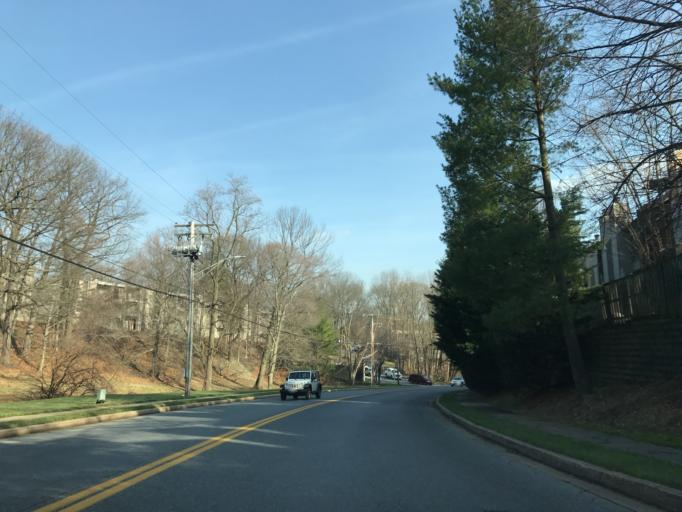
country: US
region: Maryland
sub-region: Baltimore County
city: Lutherville
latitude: 39.3762
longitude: -76.6616
